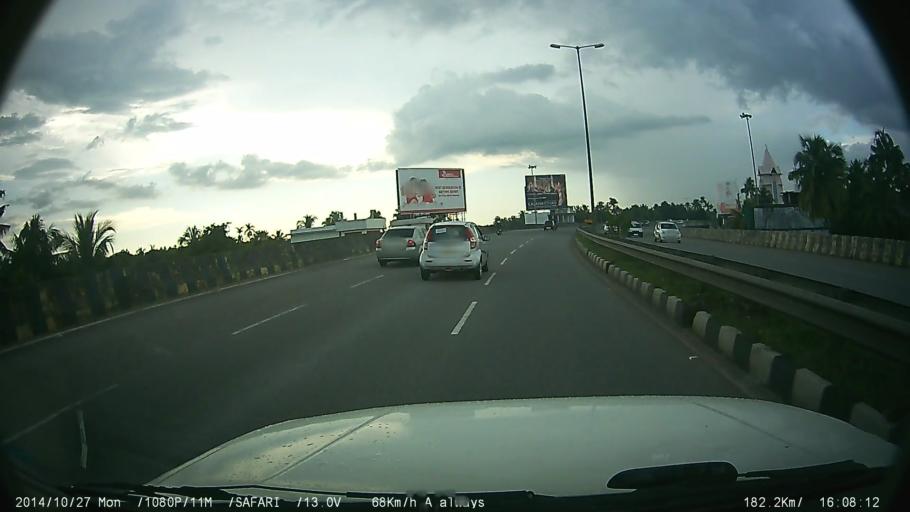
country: IN
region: Kerala
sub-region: Thrissur District
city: Kizhake Chalakudi
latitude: 10.3708
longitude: 76.3055
